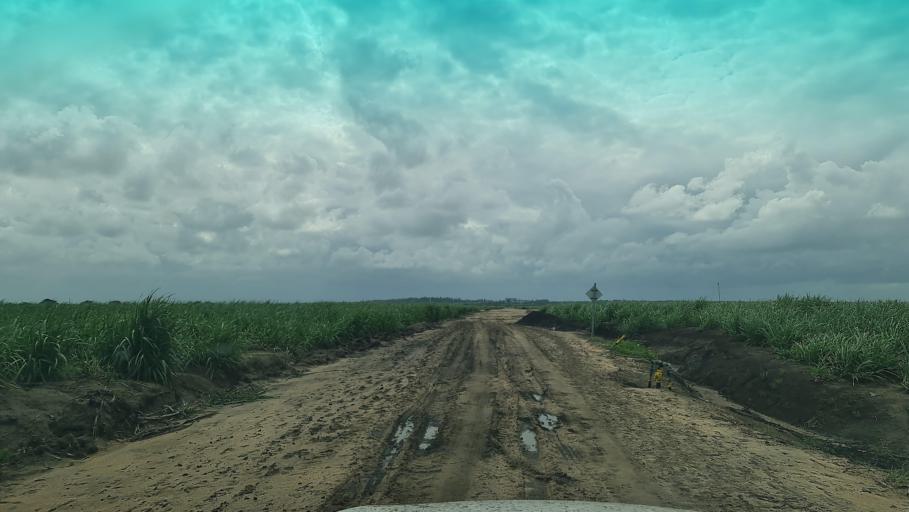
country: MZ
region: Maputo
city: Manhica
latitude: -25.4524
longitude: 32.8211
